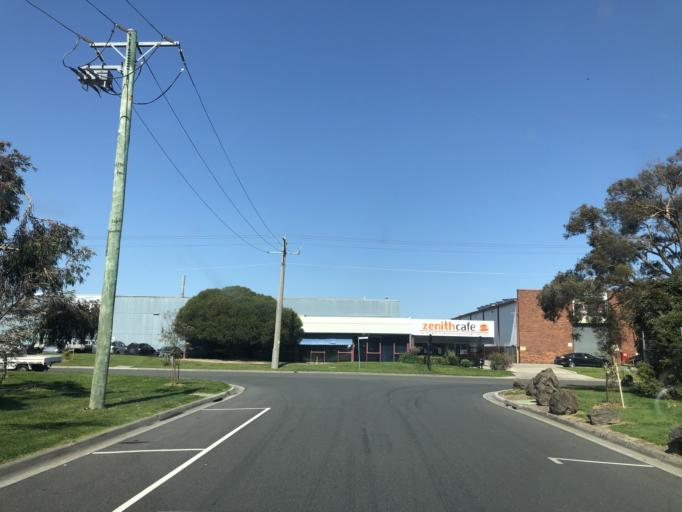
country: AU
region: Victoria
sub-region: Casey
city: Doveton
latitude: -38.0197
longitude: 145.2210
